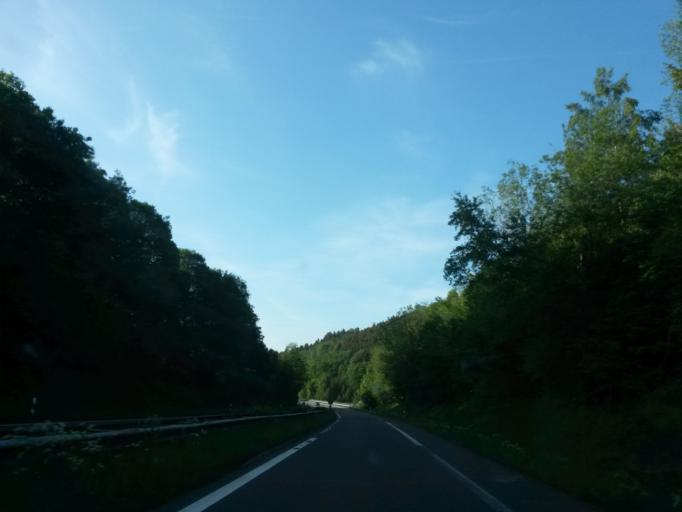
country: DE
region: North Rhine-Westphalia
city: Bergneustadt
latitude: 51.0016
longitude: 7.6374
